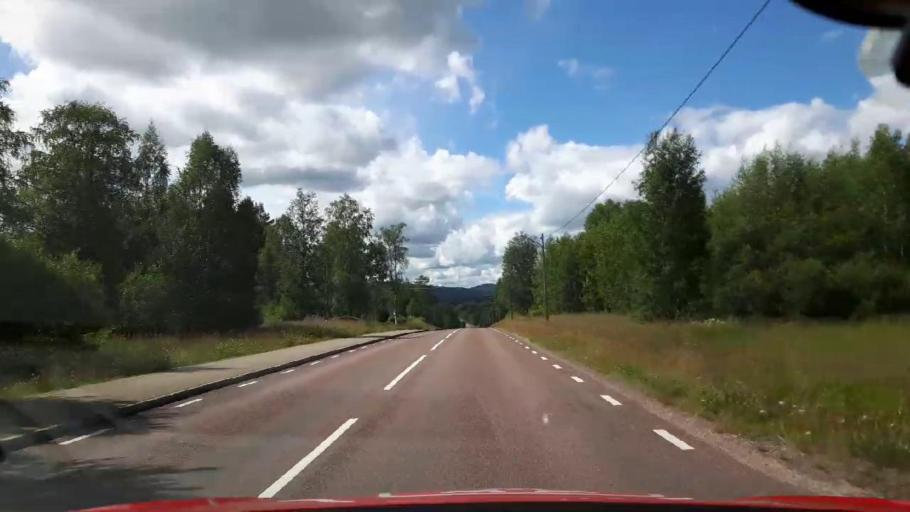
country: SE
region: Jaemtland
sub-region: Harjedalens Kommun
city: Sveg
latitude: 61.8601
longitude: 14.1046
